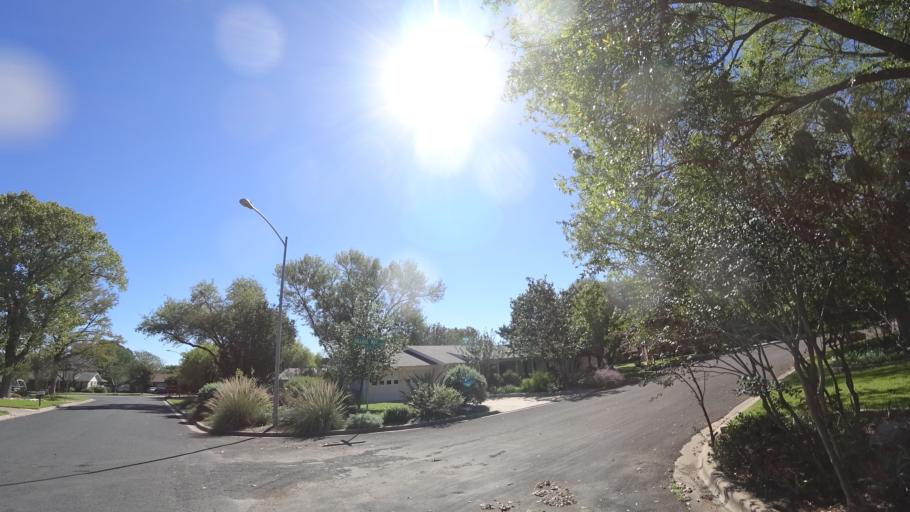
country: US
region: Texas
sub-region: Travis County
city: Rollingwood
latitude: 30.2193
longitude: -97.7986
